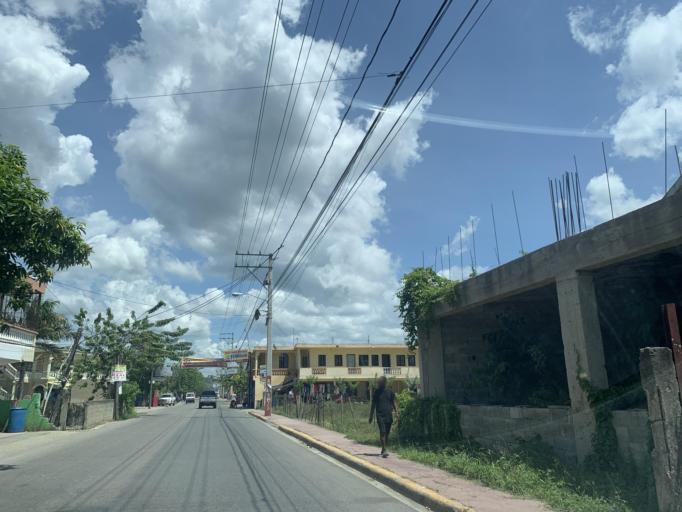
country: DO
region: Espaillat
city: Jamao al Norte
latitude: 19.6652
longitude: -70.3664
